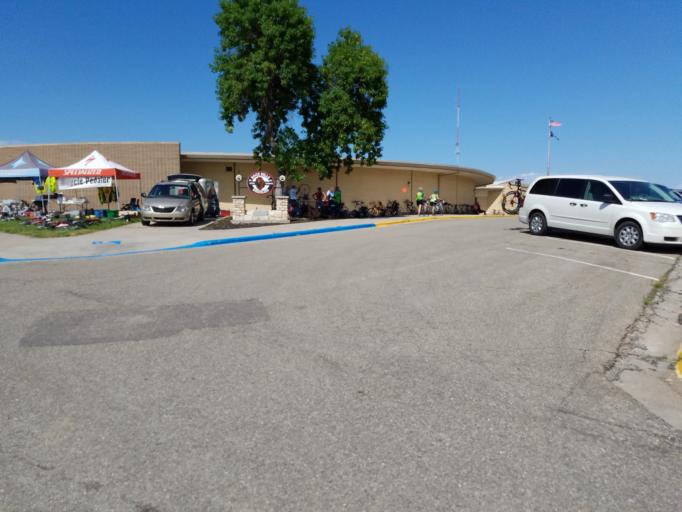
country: US
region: Kansas
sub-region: Jewell County
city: Mankato
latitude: 39.7883
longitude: -98.2025
